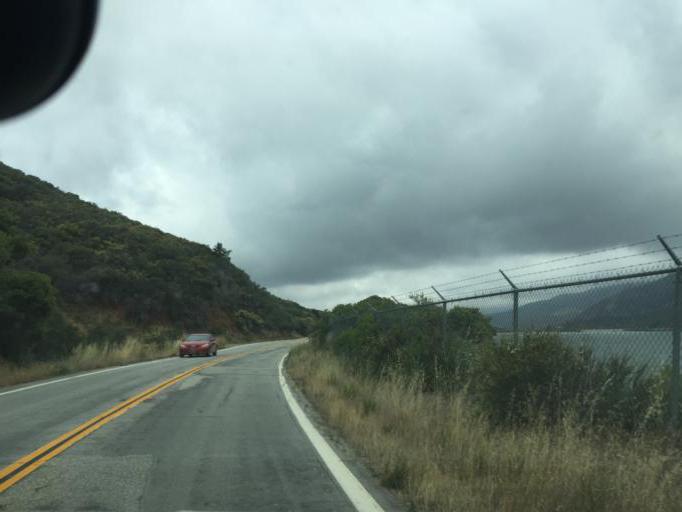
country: US
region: California
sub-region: Los Angeles County
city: Green Valley
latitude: 34.5760
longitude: -118.3763
